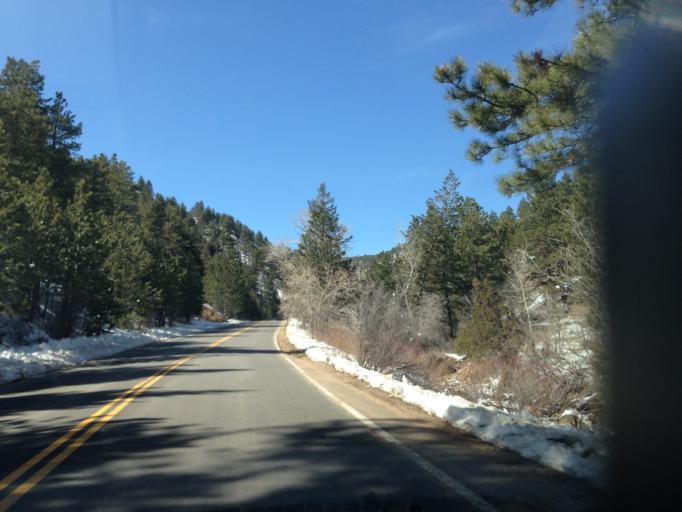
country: US
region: Colorado
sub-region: Boulder County
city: Lyons
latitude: 40.1317
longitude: -105.4072
